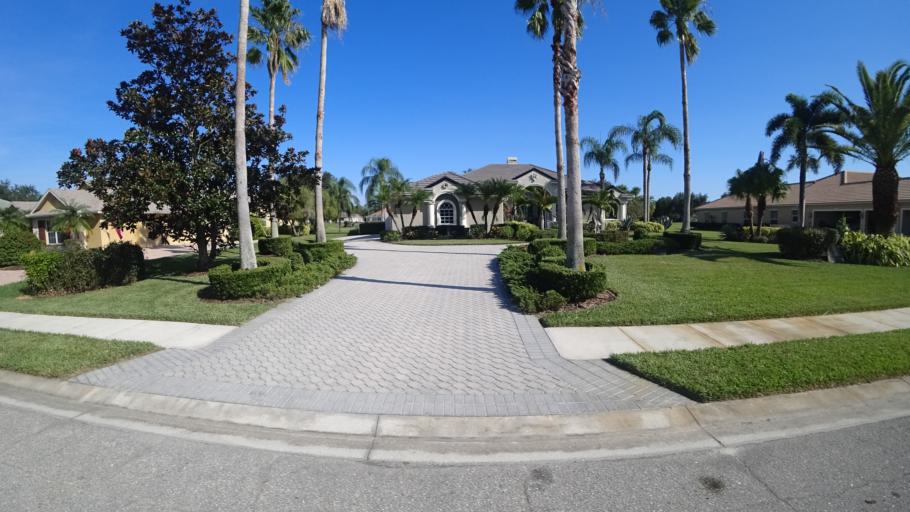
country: US
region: Florida
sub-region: Sarasota County
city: The Meadows
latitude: 27.4138
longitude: -82.4443
